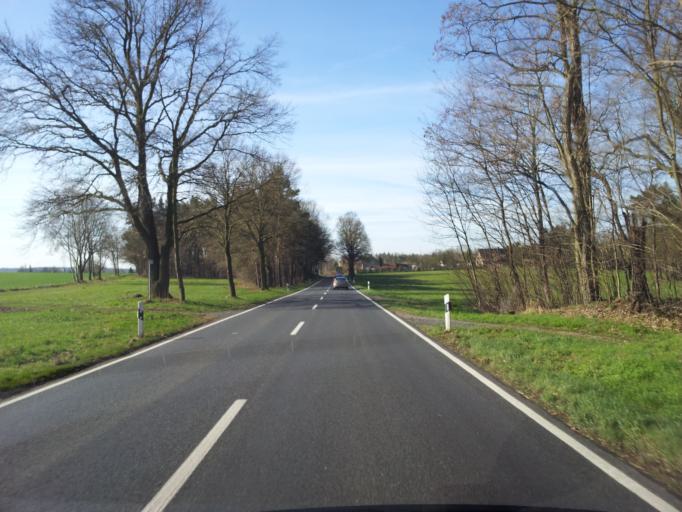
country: DE
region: Saxony
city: Konigsbruck
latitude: 51.3035
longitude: 13.9176
